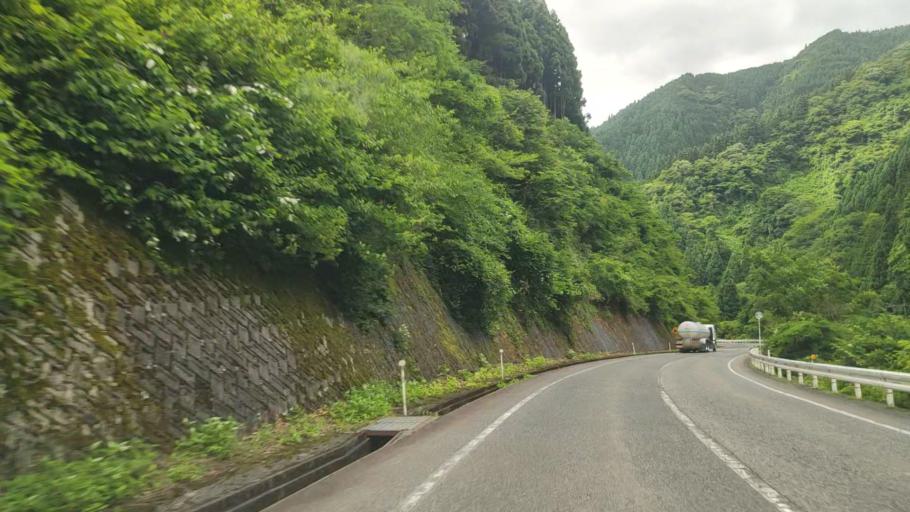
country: JP
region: Tottori
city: Yonago
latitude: 35.2575
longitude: 133.4375
